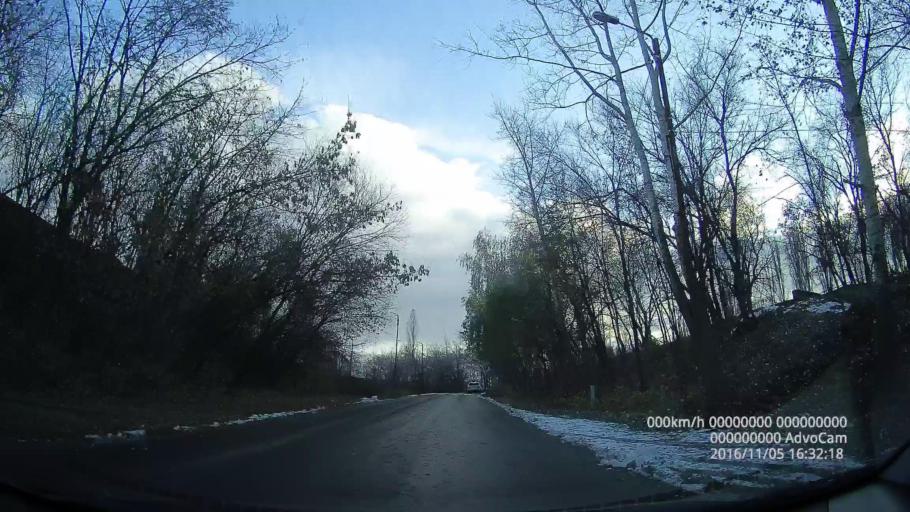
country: RU
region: Voronezj
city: Voronezh
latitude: 51.6861
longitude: 39.2176
